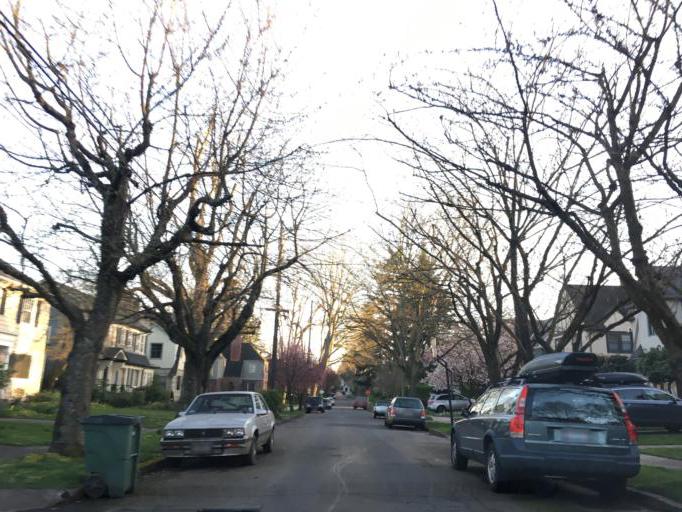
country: US
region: Oregon
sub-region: Multnomah County
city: Portland
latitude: 45.5400
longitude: -122.6345
